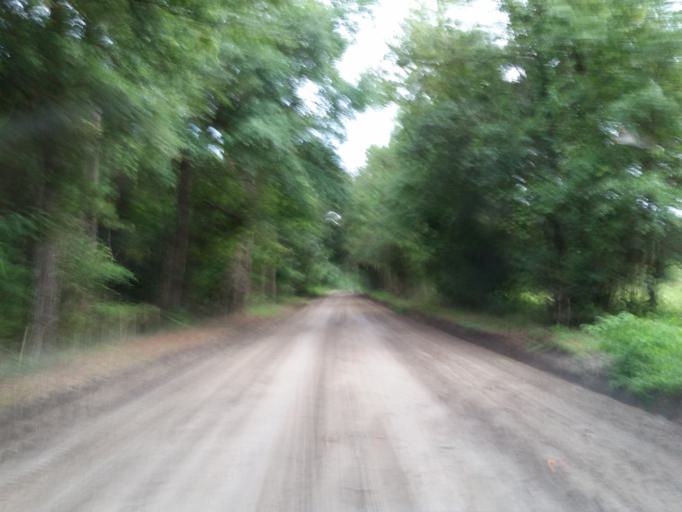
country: US
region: Florida
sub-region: Alachua County
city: High Springs
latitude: 29.9655
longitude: -82.5595
